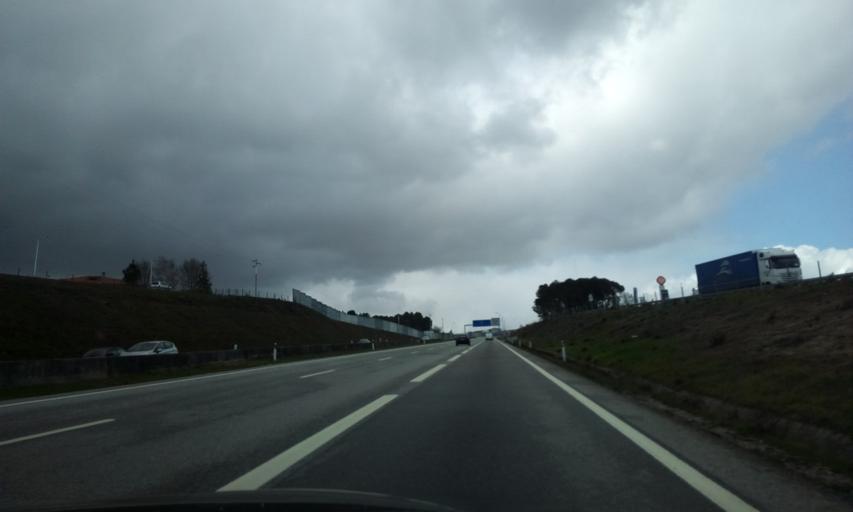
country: PT
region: Viseu
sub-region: Viseu
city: Rio de Loba
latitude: 40.6334
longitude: -7.8448
